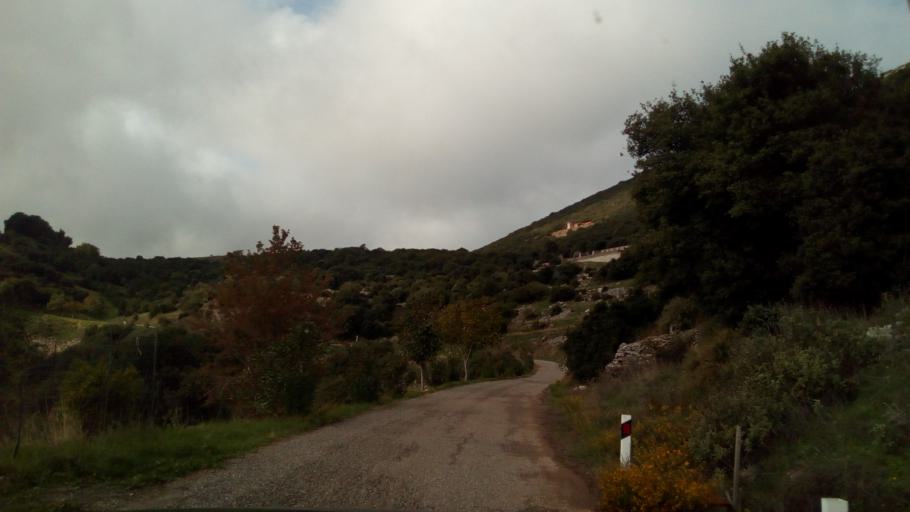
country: GR
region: West Greece
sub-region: Nomos Achaias
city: Kamarai
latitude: 38.4530
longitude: 21.9708
